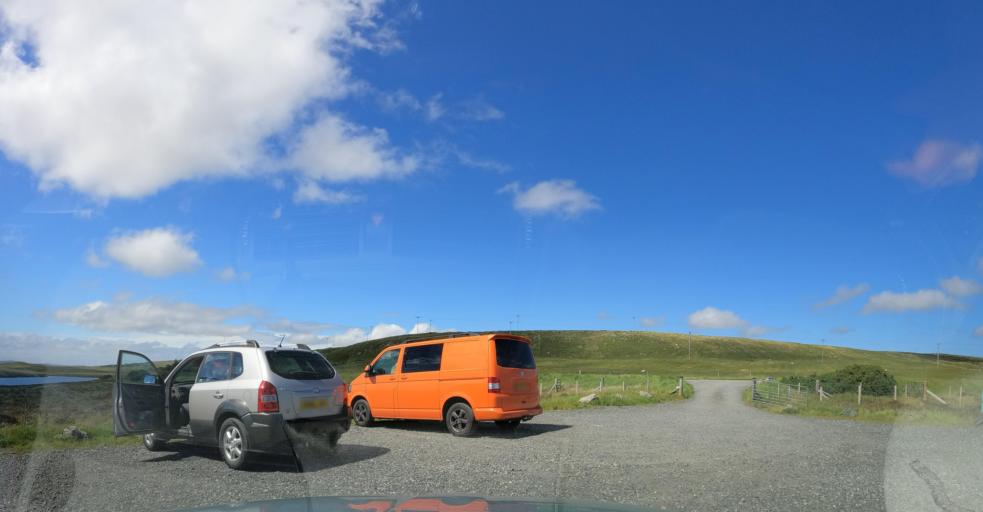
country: GB
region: Scotland
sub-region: Eilean Siar
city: Stornoway
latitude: 58.1578
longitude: -6.5234
